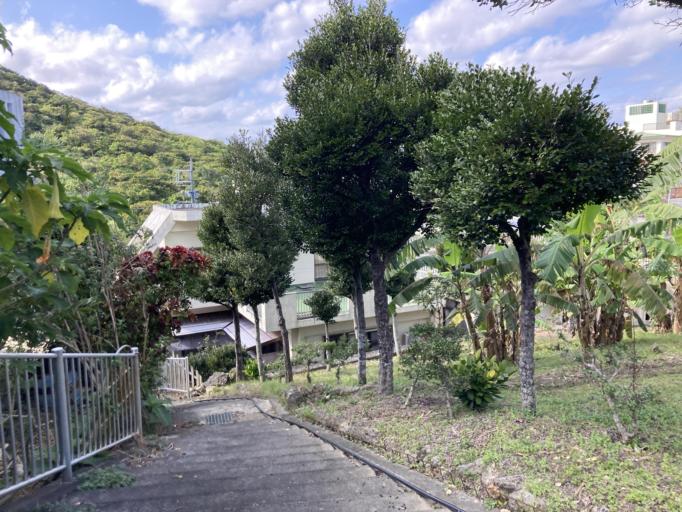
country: JP
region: Okinawa
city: Tomigusuku
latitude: 26.1863
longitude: 127.7563
